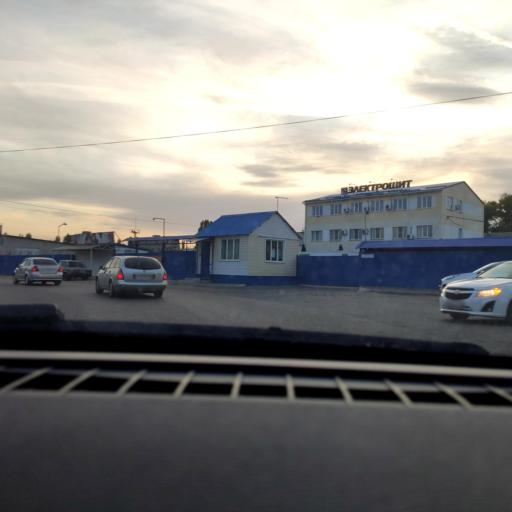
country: RU
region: Voronezj
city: Maslovka
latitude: 51.6368
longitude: 39.2791
